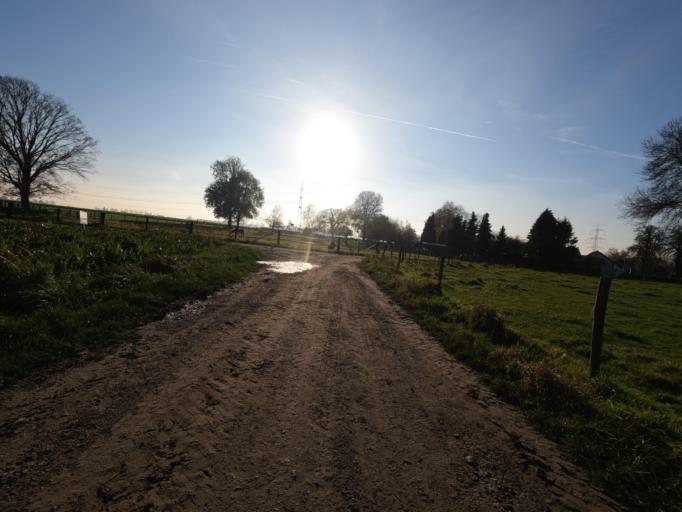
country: DE
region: North Rhine-Westphalia
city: Baesweiler
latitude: 50.9533
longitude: 6.1955
